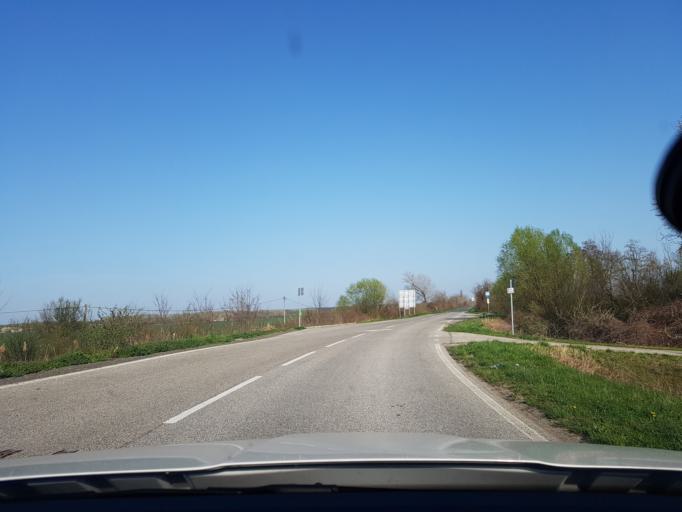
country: HU
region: Tolna
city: Ocseny
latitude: 46.3403
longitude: 18.7624
